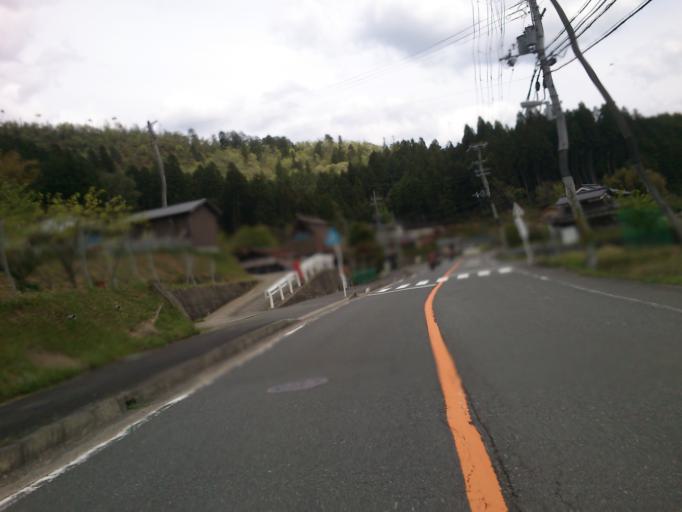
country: JP
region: Kyoto
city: Kameoka
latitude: 35.2136
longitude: 135.5568
